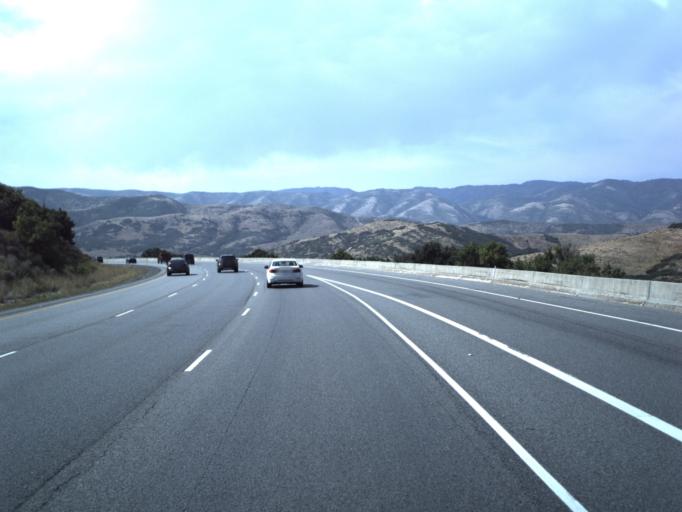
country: US
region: Utah
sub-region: Summit County
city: Summit Park
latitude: 40.7424
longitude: -111.6775
